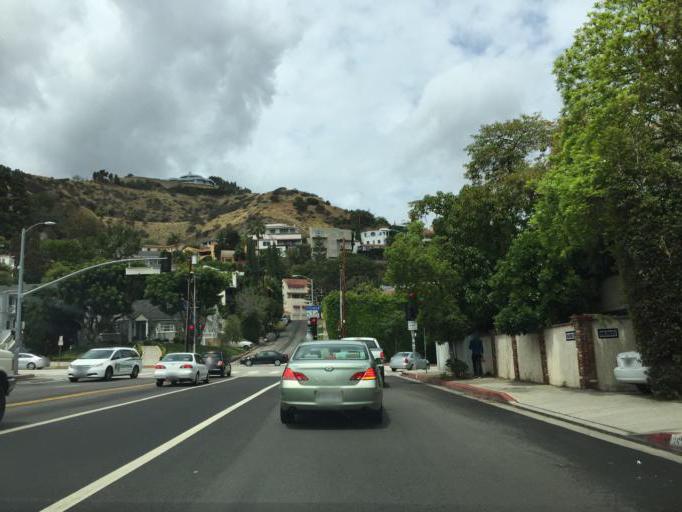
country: US
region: California
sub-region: Los Angeles County
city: West Hollywood
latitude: 34.1008
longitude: -118.3615
